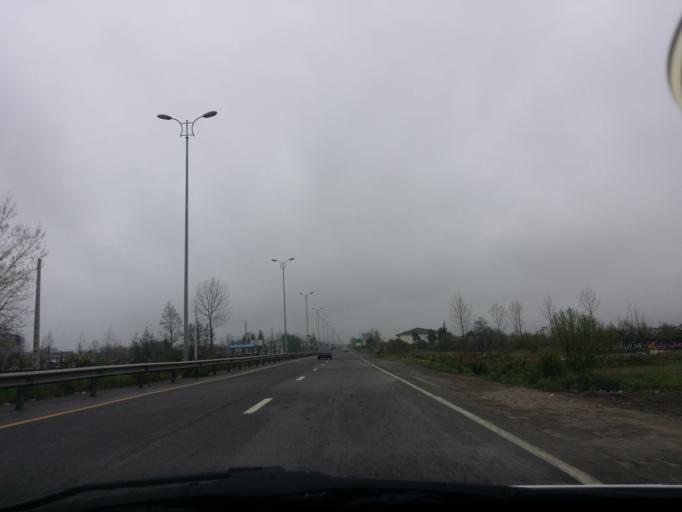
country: IR
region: Mazandaran
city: Tonekabon
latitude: 36.7990
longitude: 50.8934
